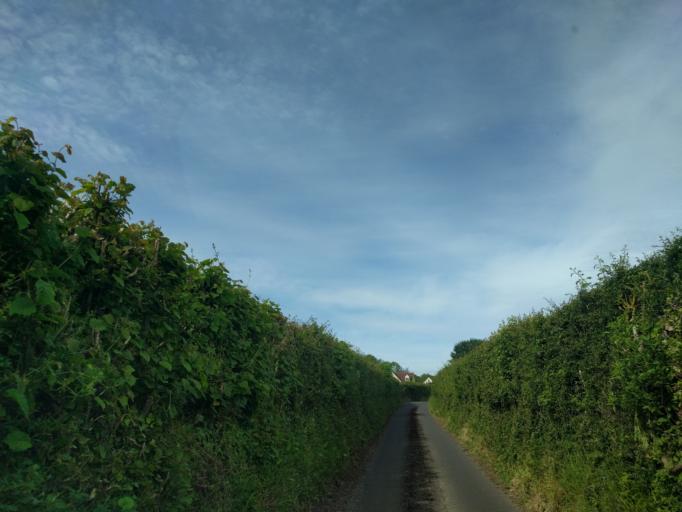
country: GB
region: England
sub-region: Wiltshire
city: Melksham
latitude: 51.3325
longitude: -2.1277
